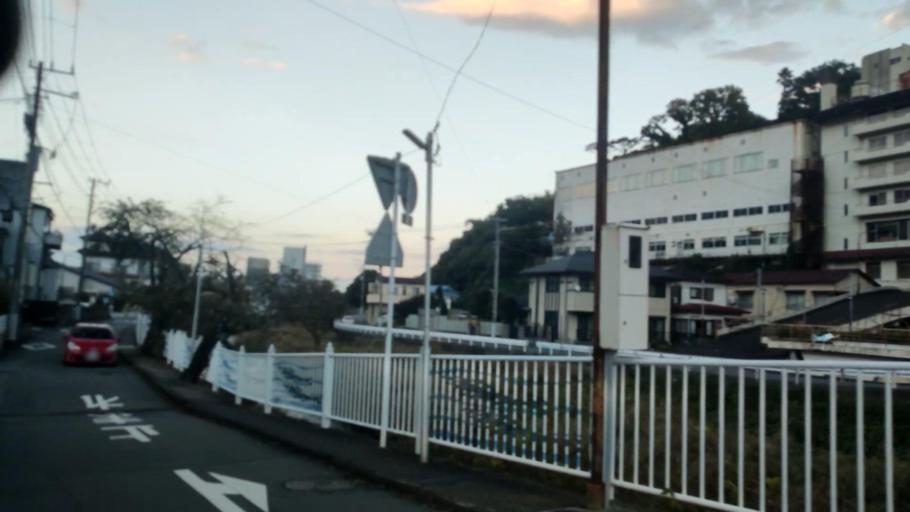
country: JP
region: Shizuoka
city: Ito
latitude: 34.9614
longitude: 139.0918
